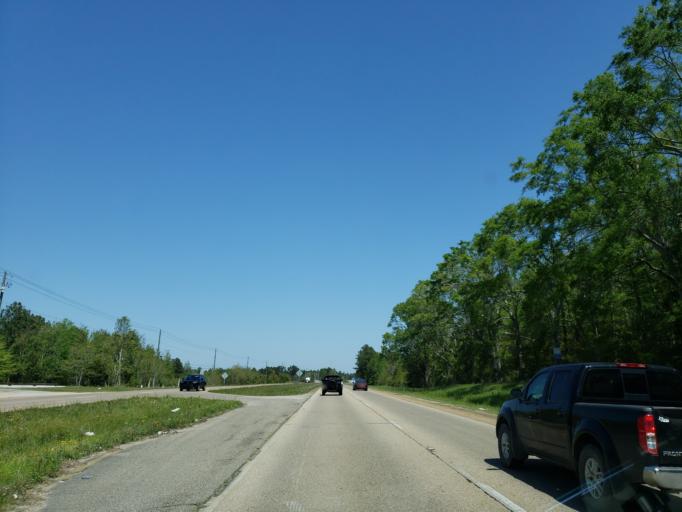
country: US
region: Mississippi
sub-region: Harrison County
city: Lyman
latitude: 30.5043
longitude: -89.1074
